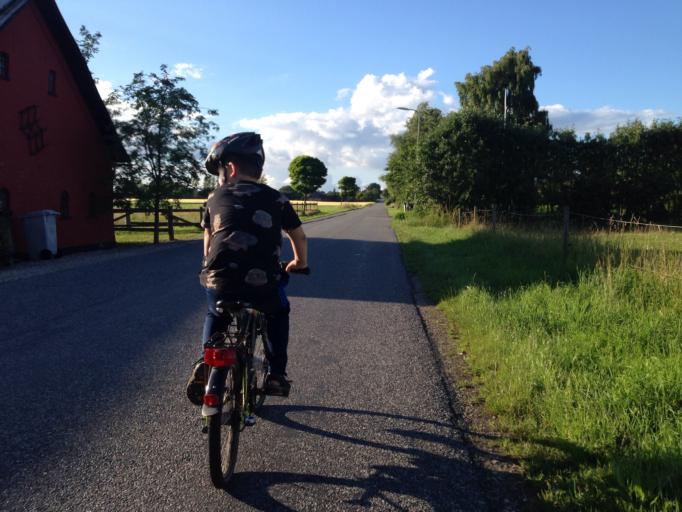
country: DK
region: South Denmark
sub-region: Middelfart Kommune
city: Norre Aby
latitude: 55.4749
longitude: 9.9034
